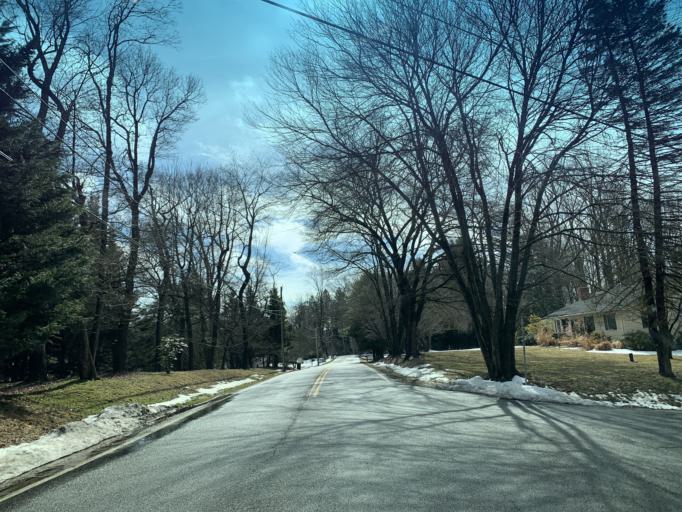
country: US
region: Delaware
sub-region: New Castle County
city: Newark
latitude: 39.7120
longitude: -75.8003
